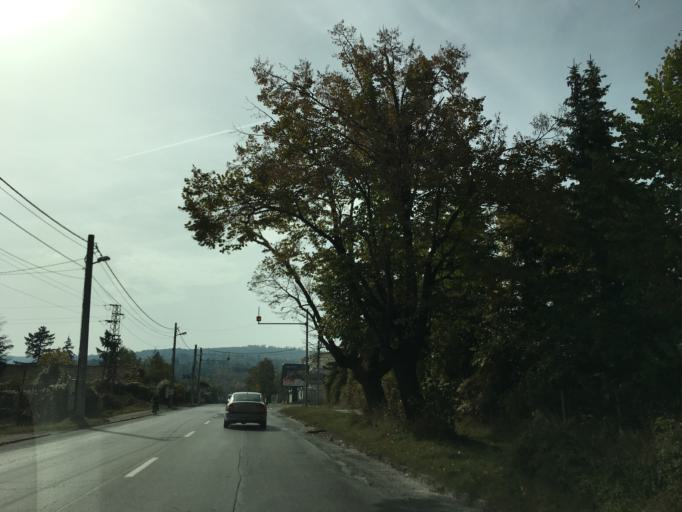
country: BG
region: Sofia-Capital
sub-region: Stolichna Obshtina
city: Sofia
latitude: 42.6169
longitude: 23.4018
